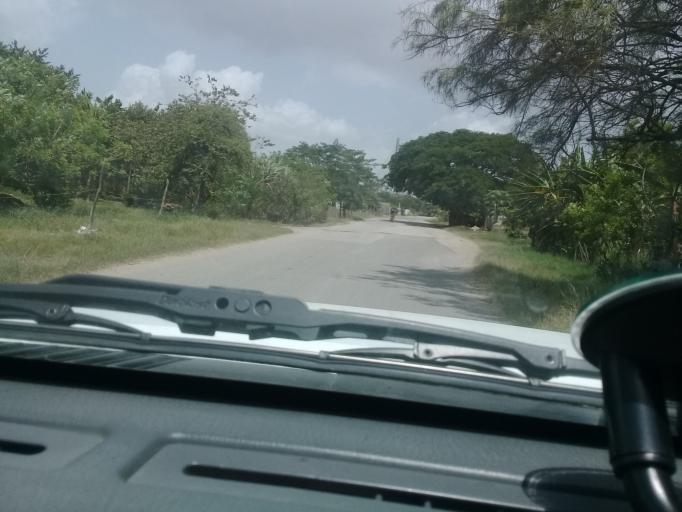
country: MX
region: Veracruz
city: Anahuac
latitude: 22.2239
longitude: -97.8282
